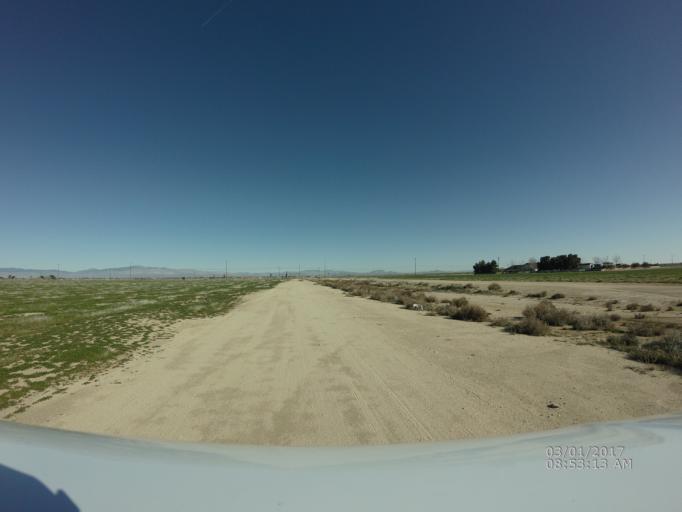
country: US
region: California
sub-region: Los Angeles County
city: Quartz Hill
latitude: 34.7314
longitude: -118.2725
